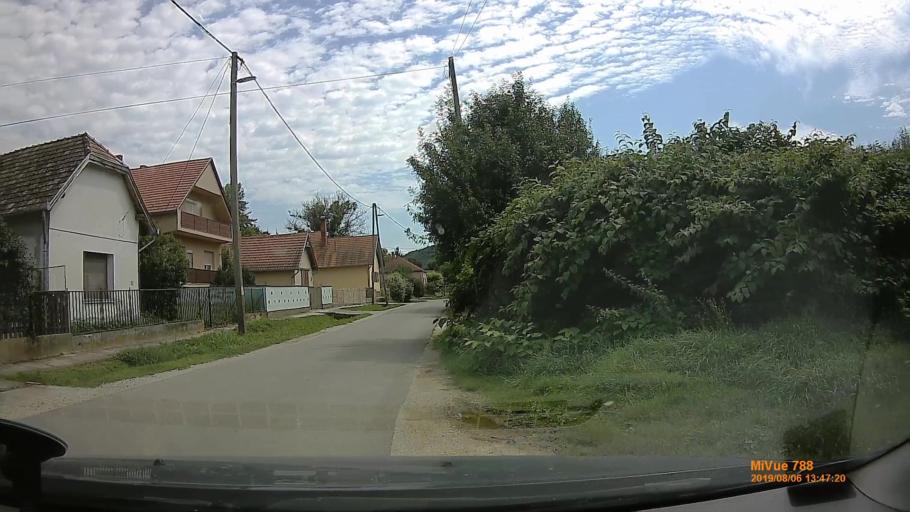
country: HU
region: Zala
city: Zalakomar
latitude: 46.5735
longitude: 17.0977
